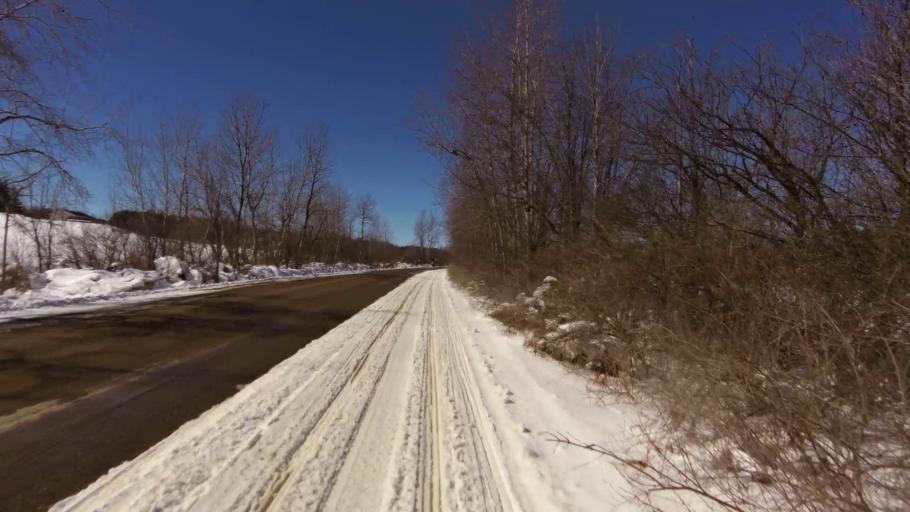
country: US
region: New York
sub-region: Cattaraugus County
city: Delevan
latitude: 42.4346
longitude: -78.4061
